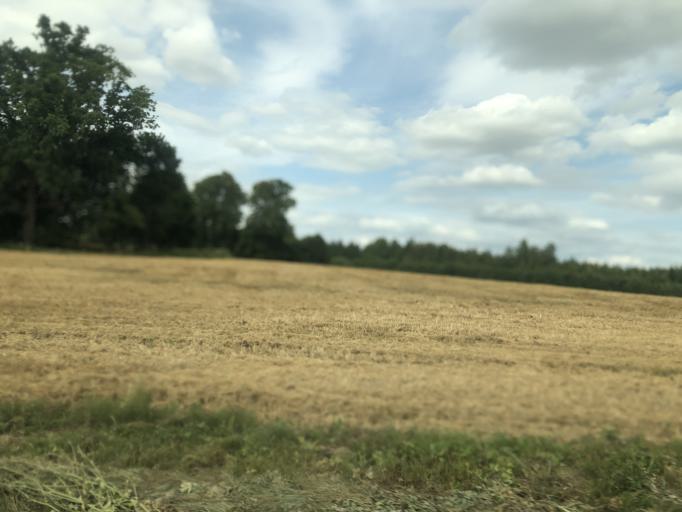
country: LV
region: Vecumnieki
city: Vecumnieki
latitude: 56.4582
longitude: 24.6553
